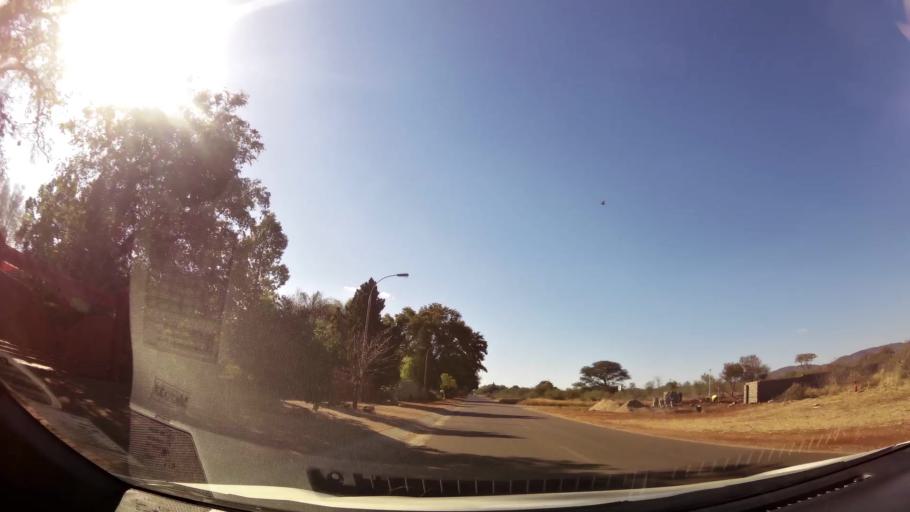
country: ZA
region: Limpopo
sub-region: Waterberg District Municipality
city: Mokopane
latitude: -24.1946
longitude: 28.9954
